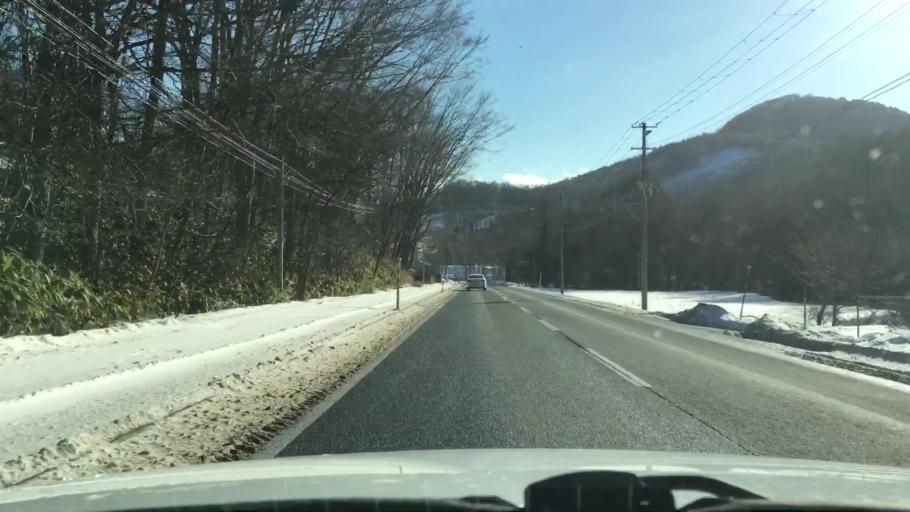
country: JP
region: Iwate
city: Morioka-shi
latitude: 39.6434
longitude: 141.3750
